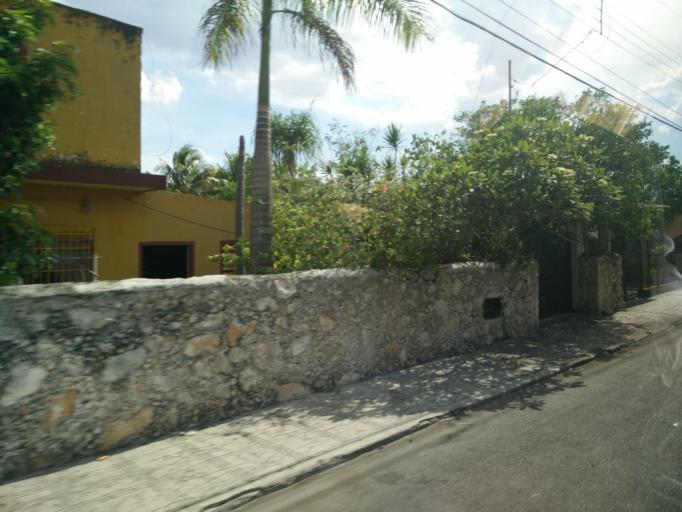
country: MX
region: Yucatan
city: Merida
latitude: 20.9650
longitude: -89.6016
